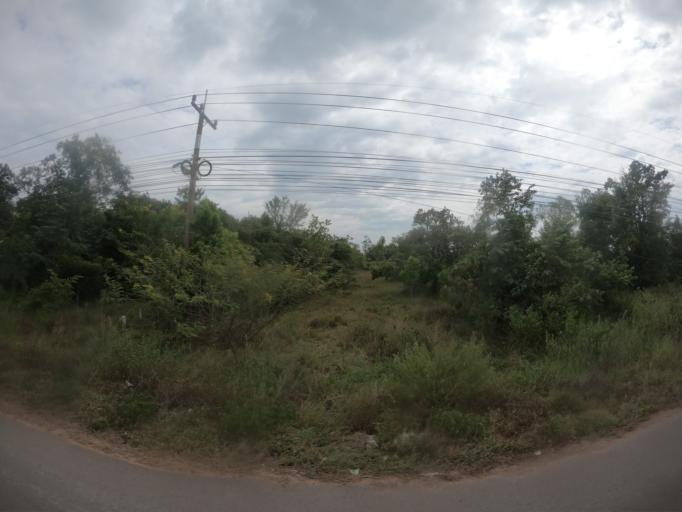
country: TH
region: Maha Sarakham
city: Kantharawichai
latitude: 16.2818
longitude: 103.2917
